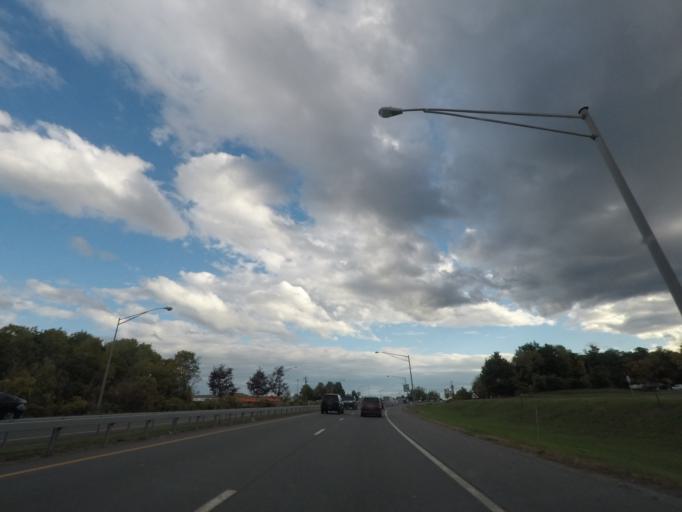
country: US
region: New York
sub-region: Albany County
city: McKownville
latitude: 42.7003
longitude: -73.8513
